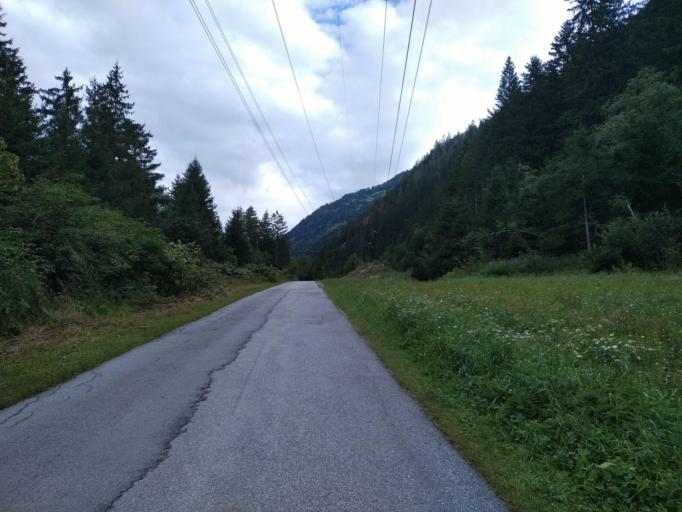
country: AT
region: Tyrol
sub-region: Politischer Bezirk Lienz
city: Hopfgarten in Defereggen
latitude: 46.9369
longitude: 12.5756
